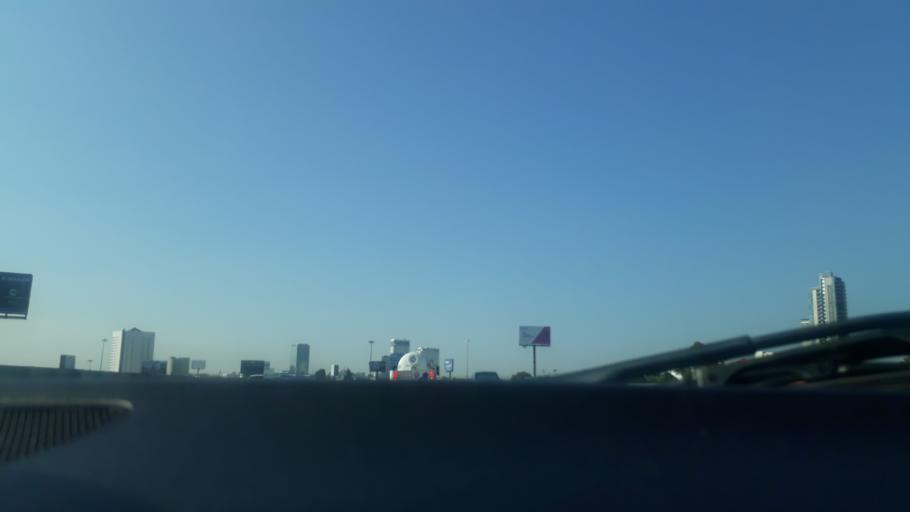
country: MX
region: Puebla
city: Tlazcalancingo
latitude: 19.0072
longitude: -98.2602
